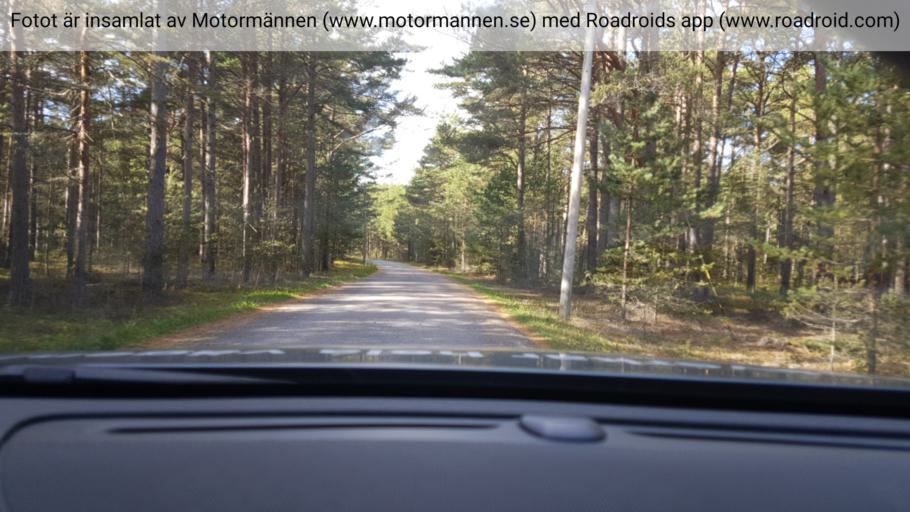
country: SE
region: Gotland
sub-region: Gotland
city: Slite
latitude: 57.9600
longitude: 19.3403
